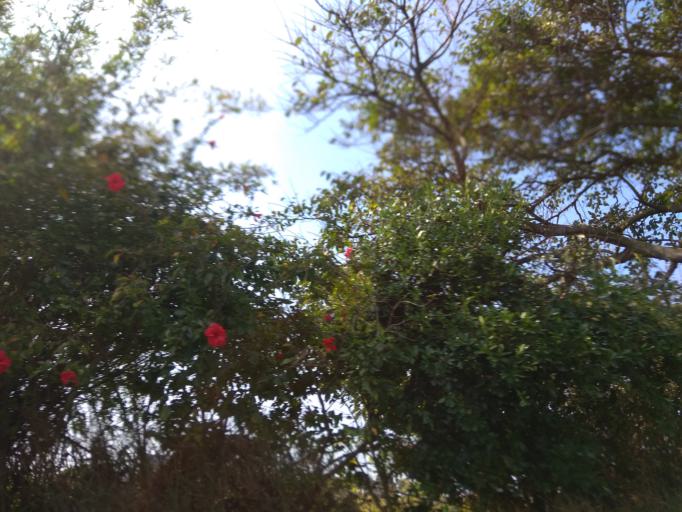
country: TW
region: Taiwan
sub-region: Hsinchu
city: Zhubei
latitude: 25.0007
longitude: 121.0448
